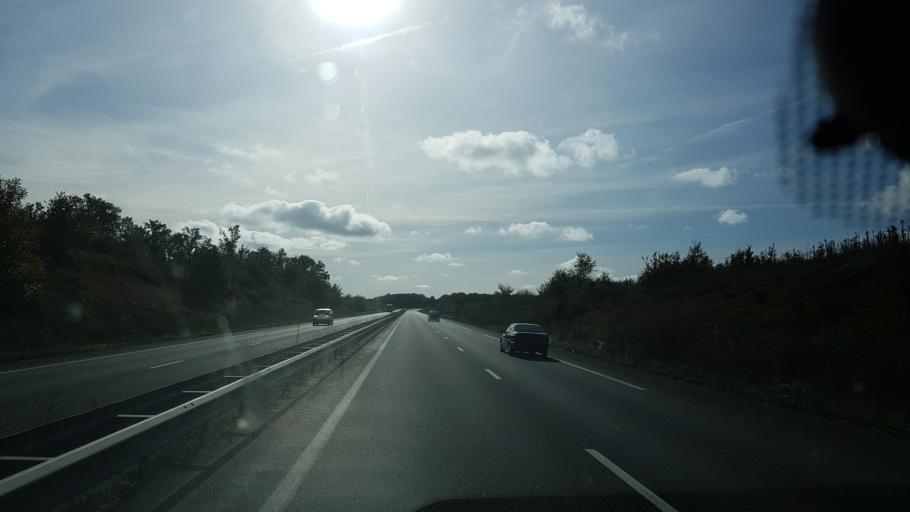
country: FR
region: Poitou-Charentes
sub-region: Departement de la Charente
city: Chasseneuil-sur-Bonnieure
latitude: 45.8009
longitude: 0.4381
